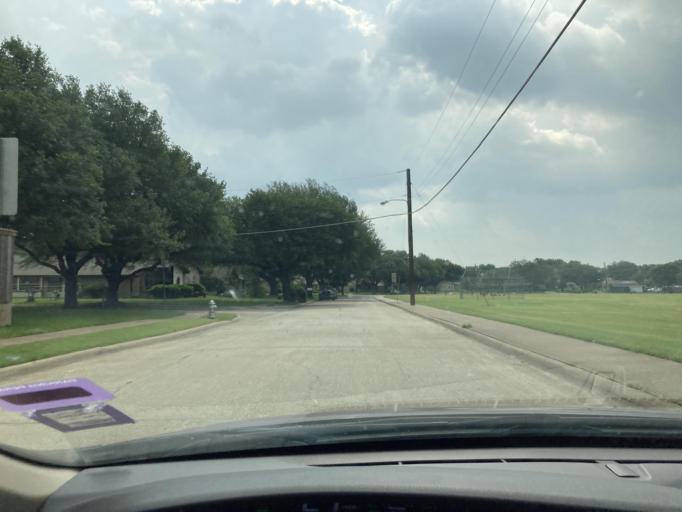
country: US
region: Texas
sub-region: Collin County
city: Plano
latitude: 33.0526
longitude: -96.7237
